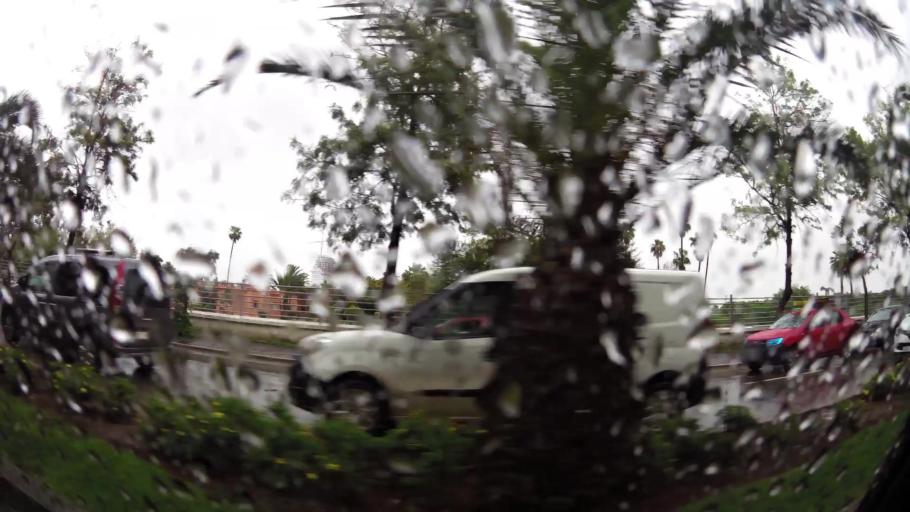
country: MA
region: Grand Casablanca
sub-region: Casablanca
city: Casablanca
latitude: 33.5601
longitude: -7.6694
